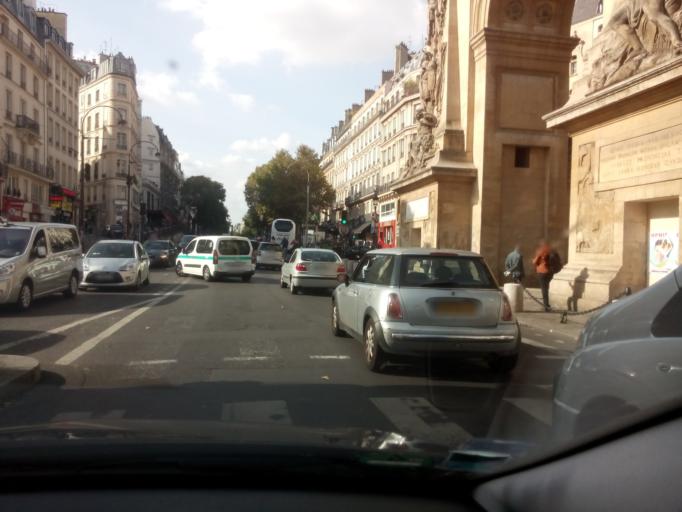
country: FR
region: Ile-de-France
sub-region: Paris
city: Paris
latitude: 48.8697
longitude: 2.3529
